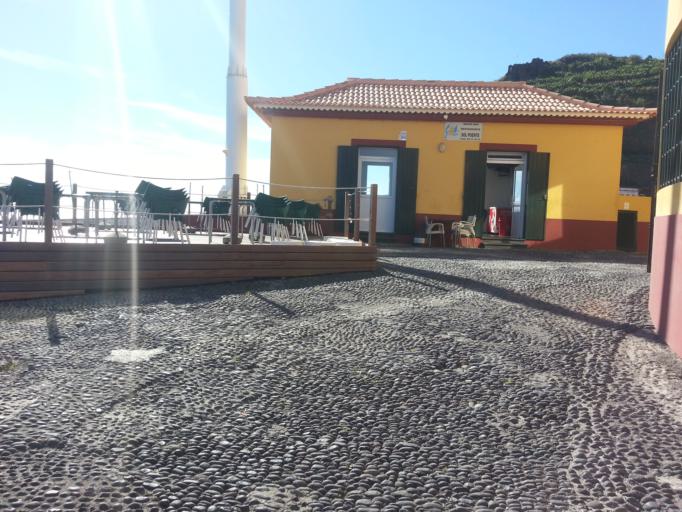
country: PT
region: Madeira
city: Ponta do Sol
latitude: 32.6785
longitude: -17.1041
